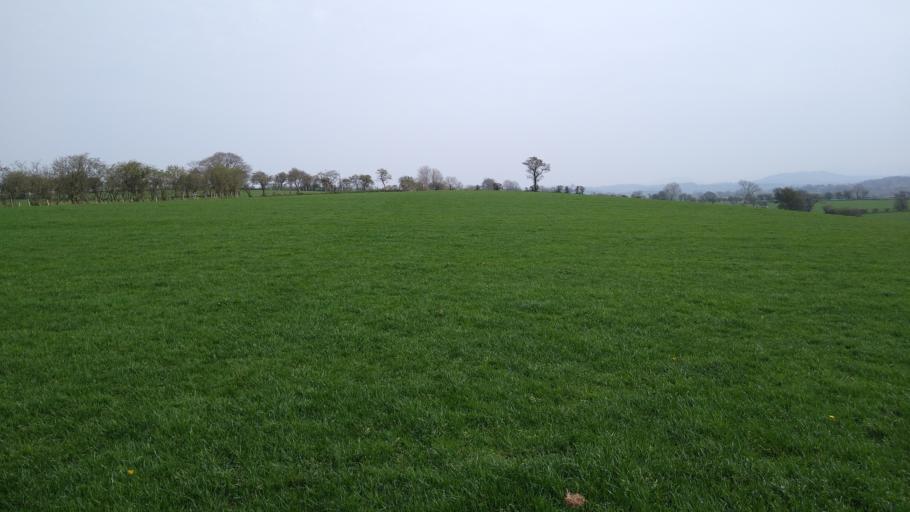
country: GB
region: England
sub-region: Cumbria
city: Dearham
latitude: 54.6611
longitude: -3.4573
